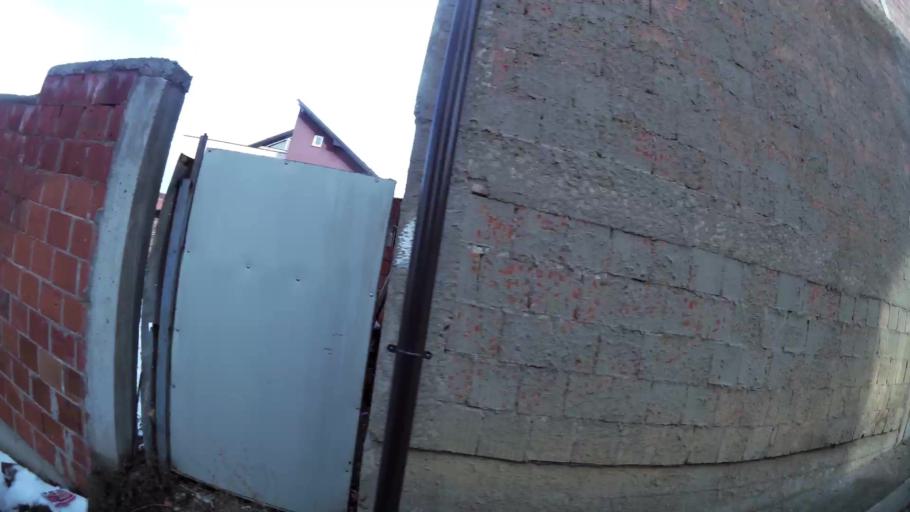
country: XK
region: Pristina
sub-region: Komuna e Prishtines
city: Pristina
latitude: 42.6757
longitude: 21.1537
